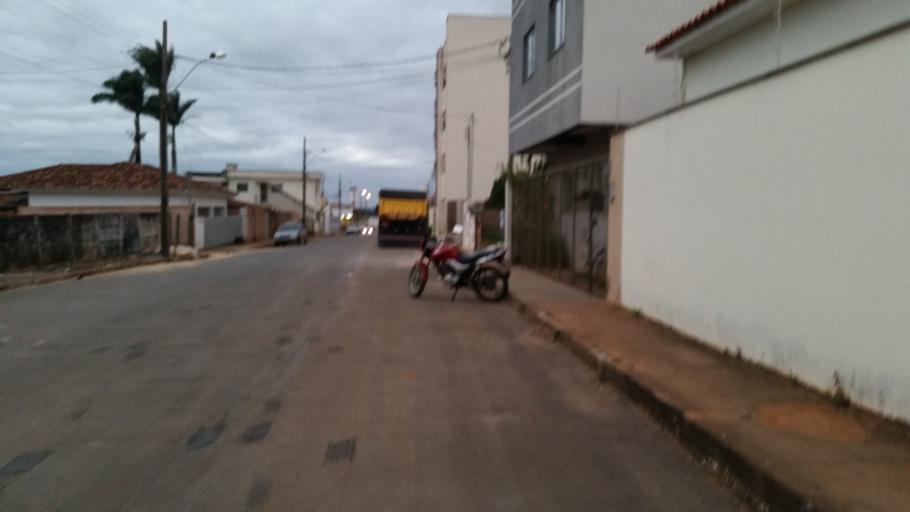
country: BR
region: Minas Gerais
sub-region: Carmo Do Paranaiba
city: Carmo do Paranaiba
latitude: -19.1990
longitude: -46.2381
